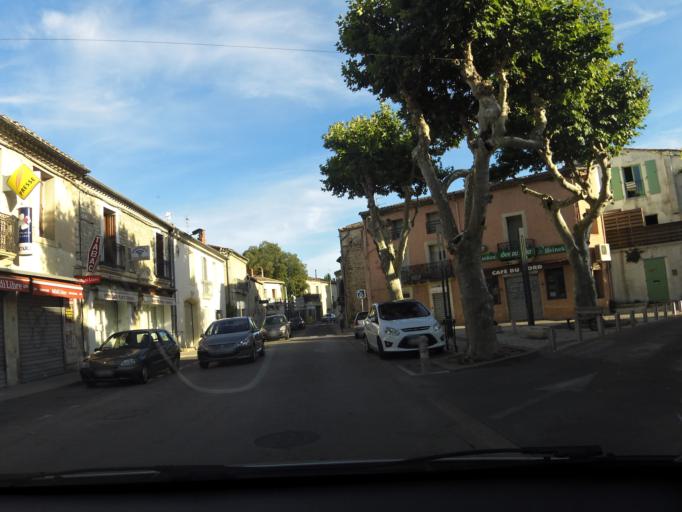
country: FR
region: Languedoc-Roussillon
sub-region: Departement de l'Herault
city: Prades-le-Lez
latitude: 43.6986
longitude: 3.8626
